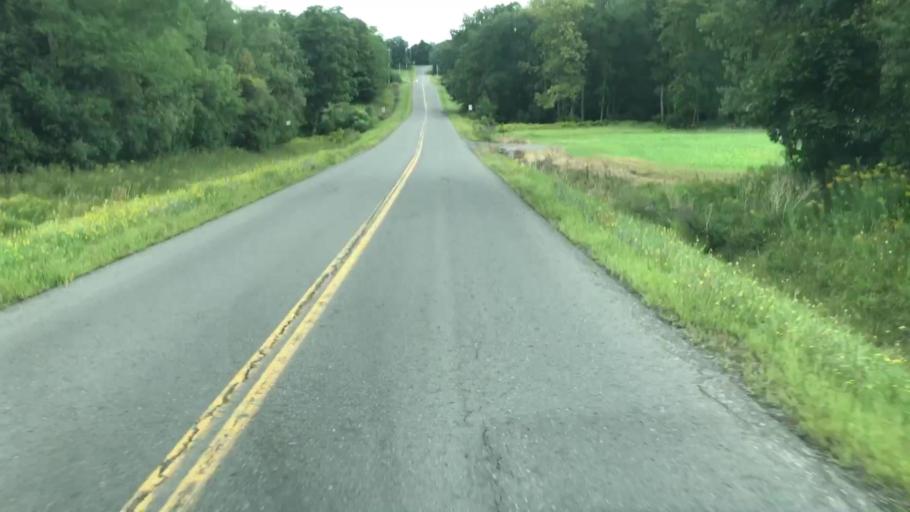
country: US
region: New York
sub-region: Cayuga County
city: Melrose Park
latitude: 42.9201
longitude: -76.4975
